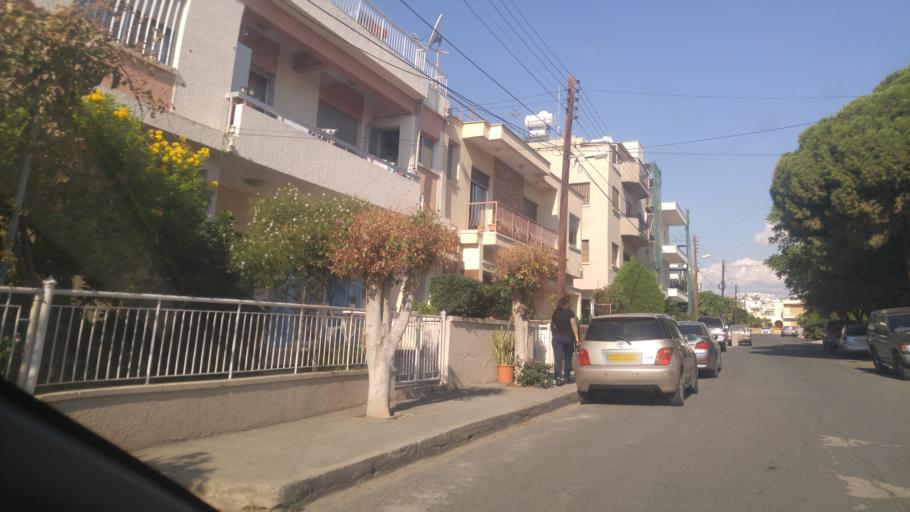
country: CY
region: Limassol
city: Limassol
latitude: 34.6948
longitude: 33.0482
